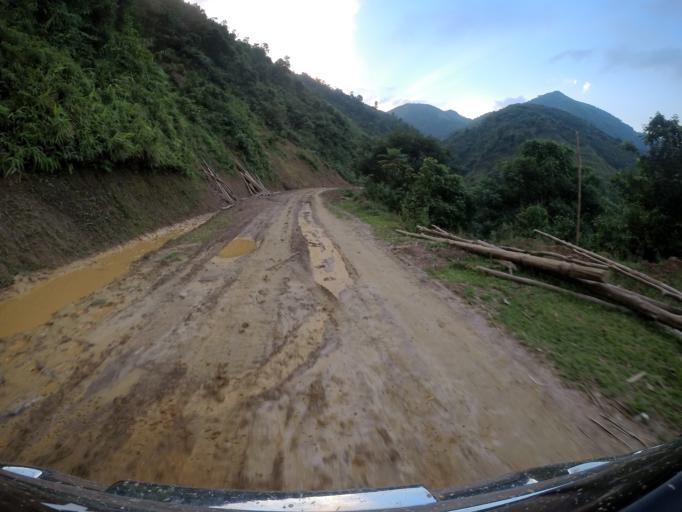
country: VN
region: Yen Bai
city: Son Thinh
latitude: 21.6940
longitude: 104.6334
